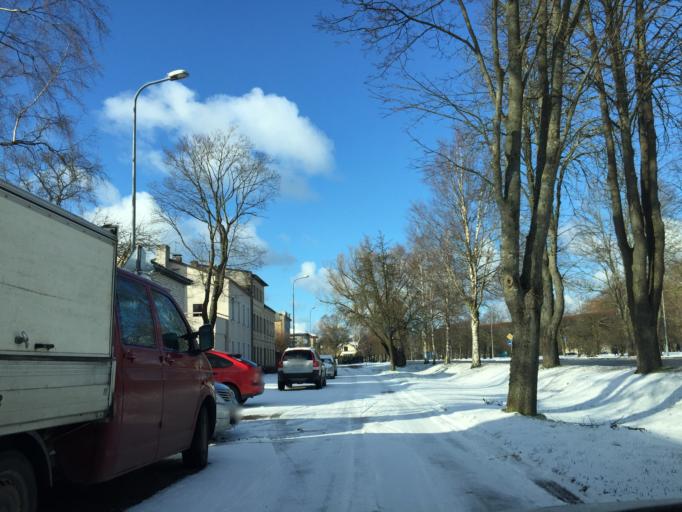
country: LV
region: Ventspils
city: Ventspils
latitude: 57.3834
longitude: 21.5661
